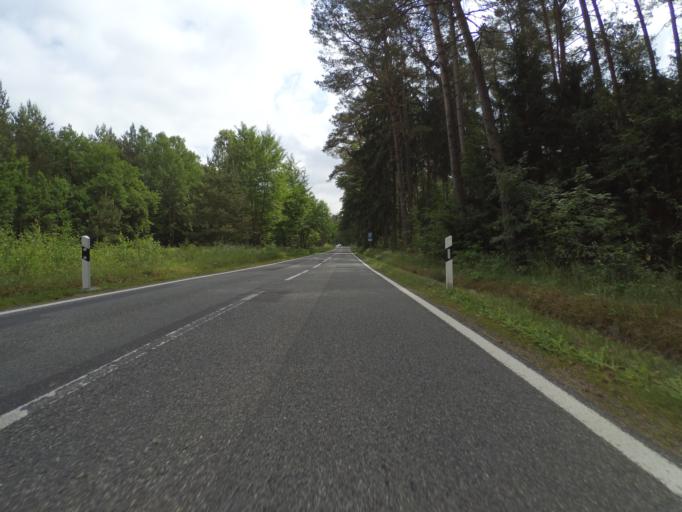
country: DE
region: Mecklenburg-Vorpommern
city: Grabowhofe
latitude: 53.5320
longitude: 12.5242
